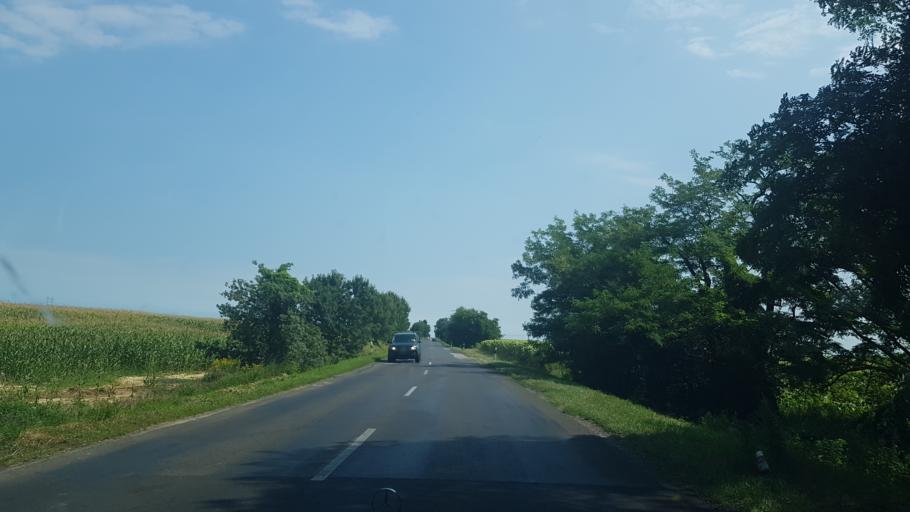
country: HU
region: Somogy
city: Bohonye
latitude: 46.4718
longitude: 17.3951
